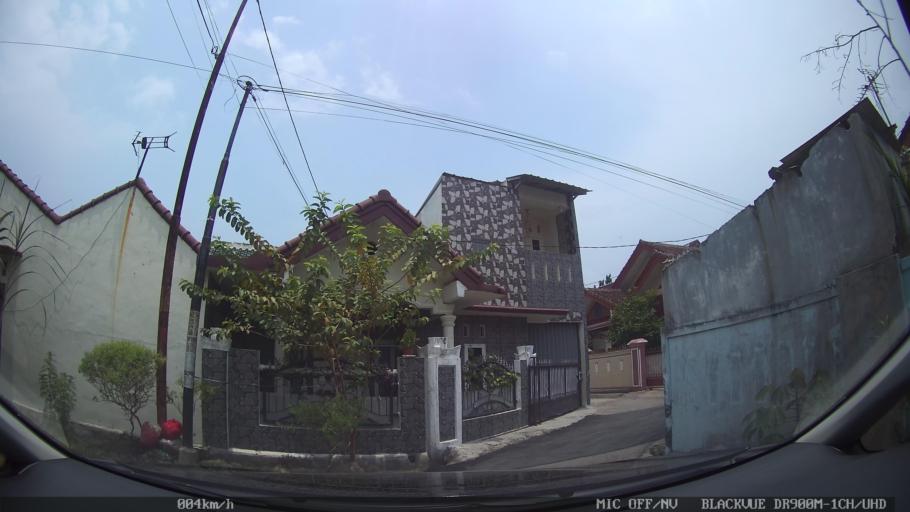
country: ID
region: Lampung
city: Kedaton
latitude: -5.3950
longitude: 105.3029
